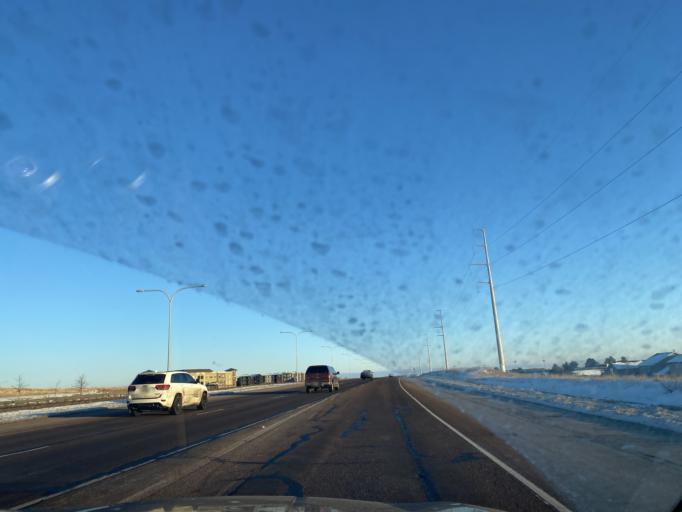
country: US
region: Colorado
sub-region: El Paso County
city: Black Forest
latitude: 38.9654
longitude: -104.7397
